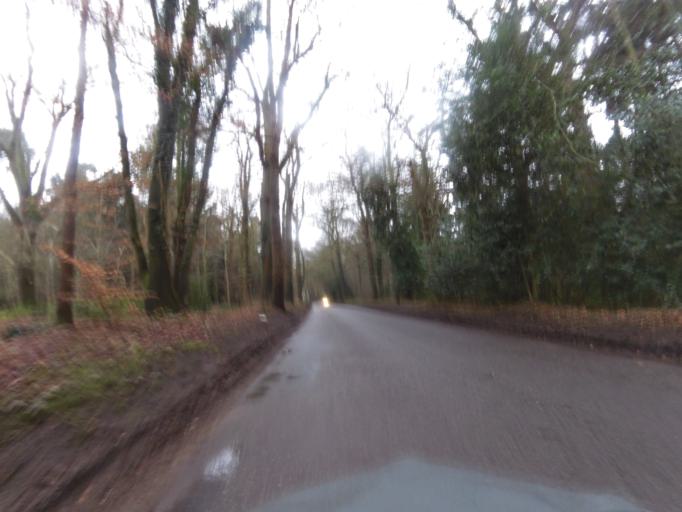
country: GB
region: England
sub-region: Norfolk
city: Briston
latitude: 52.8630
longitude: 1.0678
